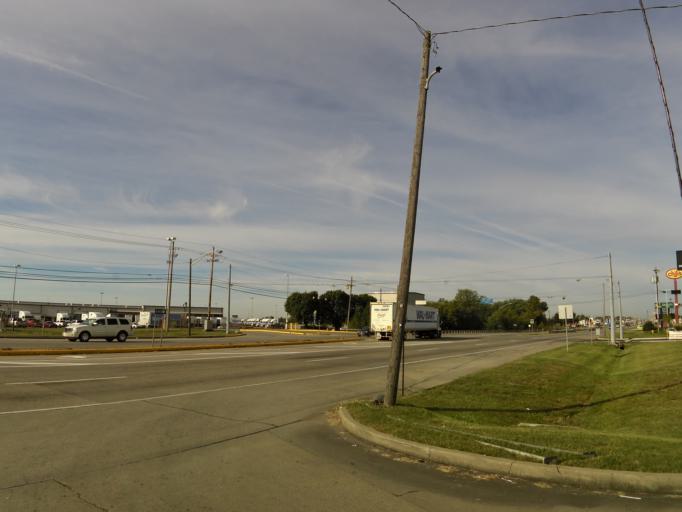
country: US
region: Indiana
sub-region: Jackson County
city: Seymour
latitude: 38.9583
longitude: -85.8493
